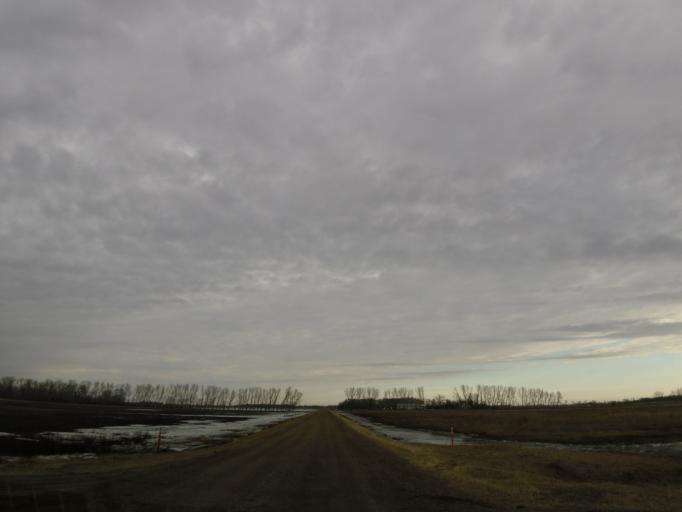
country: US
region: North Dakota
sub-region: Walsh County
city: Grafton
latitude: 48.3981
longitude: -97.4703
